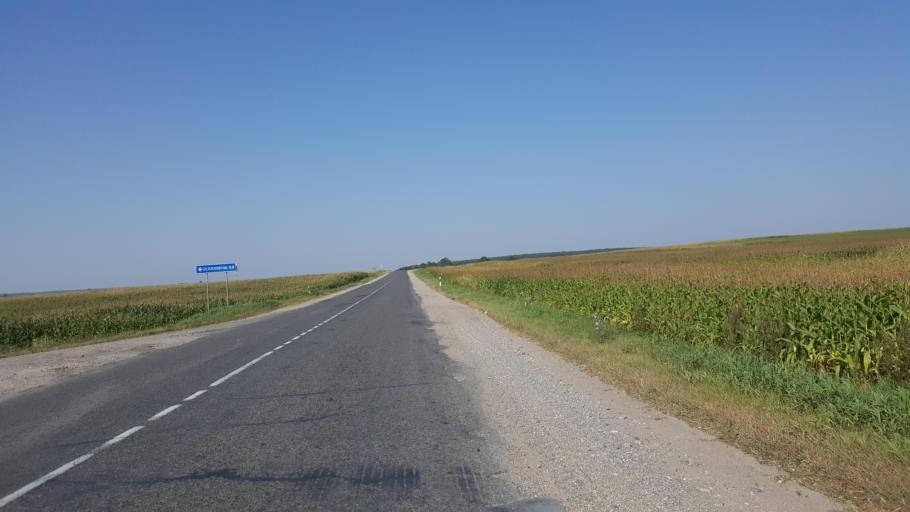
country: BY
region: Brest
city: Kamyanyets
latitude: 52.4177
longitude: 23.6775
